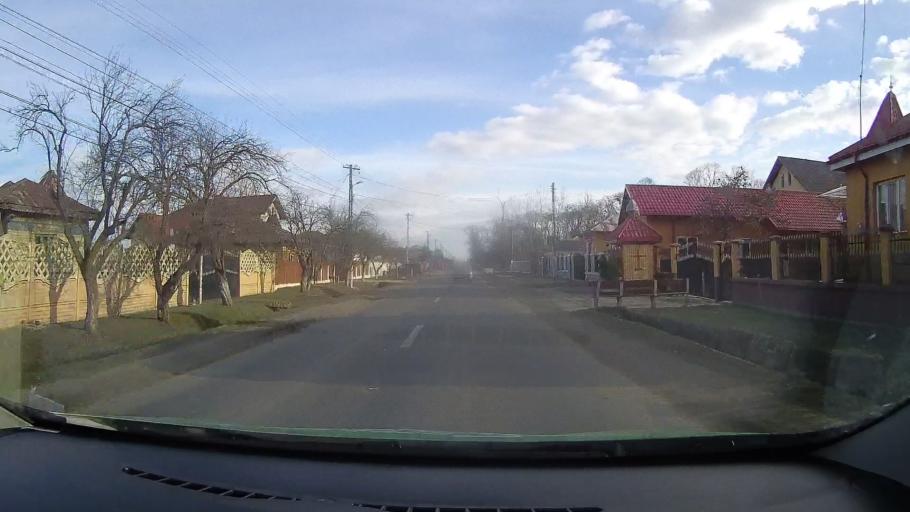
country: RO
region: Dambovita
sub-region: Comuna Vacaresti
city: Vacaresti
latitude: 44.8597
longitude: 25.4812
